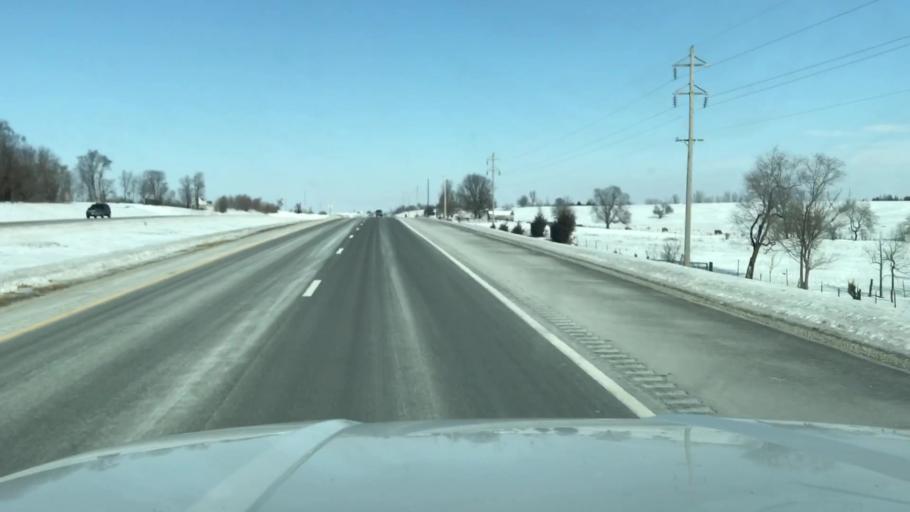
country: US
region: Missouri
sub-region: Nodaway County
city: Maryville
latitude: 40.2055
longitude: -94.8677
